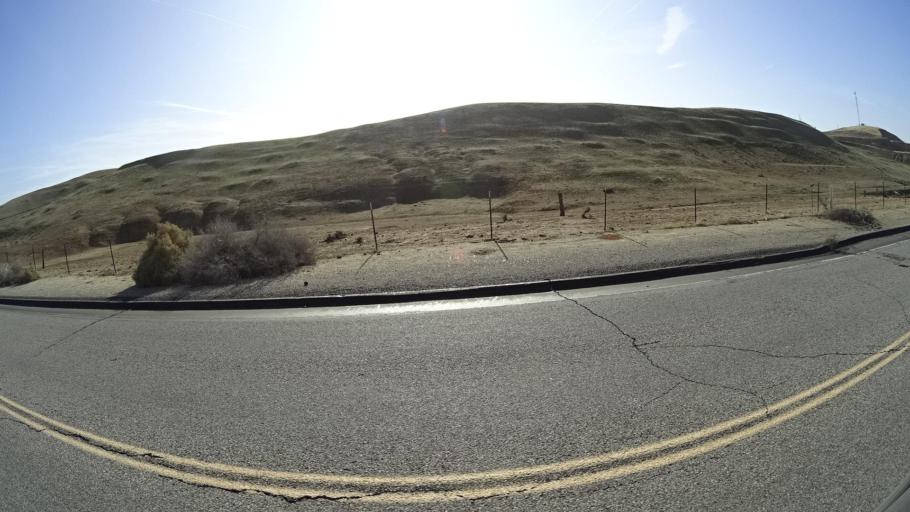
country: US
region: California
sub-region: Kern County
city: Oildale
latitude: 35.4906
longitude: -119.0001
